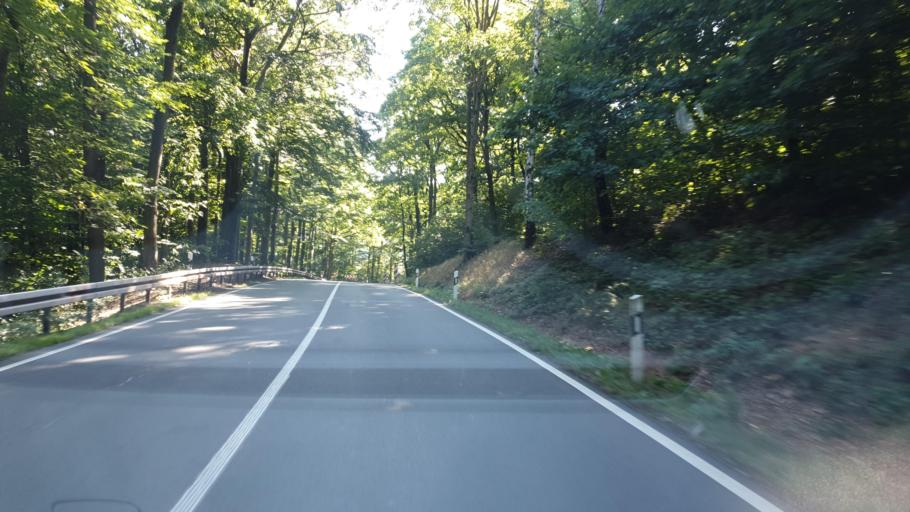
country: DE
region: Saxony
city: Aue
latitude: 50.5870
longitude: 12.7272
